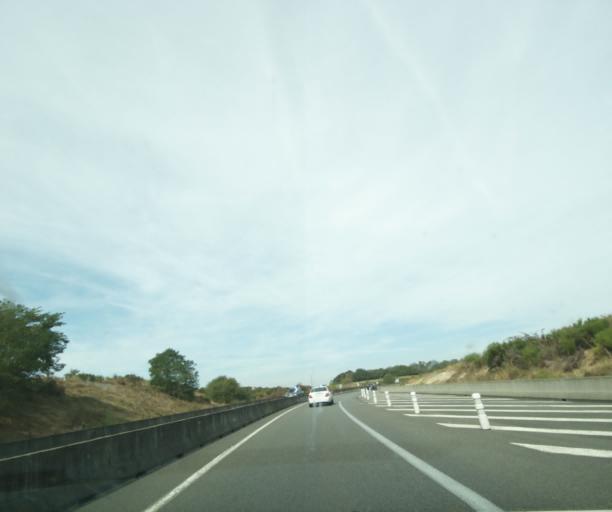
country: FR
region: Auvergne
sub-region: Departement de l'Allier
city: Lapalisse
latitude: 46.2417
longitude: 3.6187
